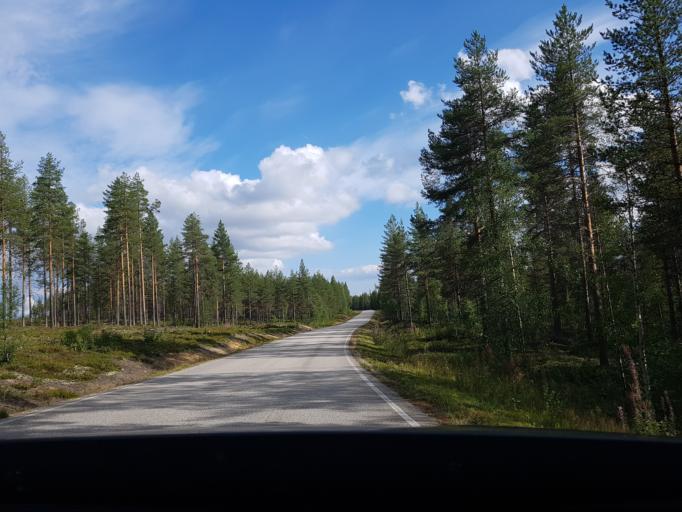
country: FI
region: Kainuu
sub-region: Kehys-Kainuu
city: Kuhmo
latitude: 64.6182
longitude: 29.7102
